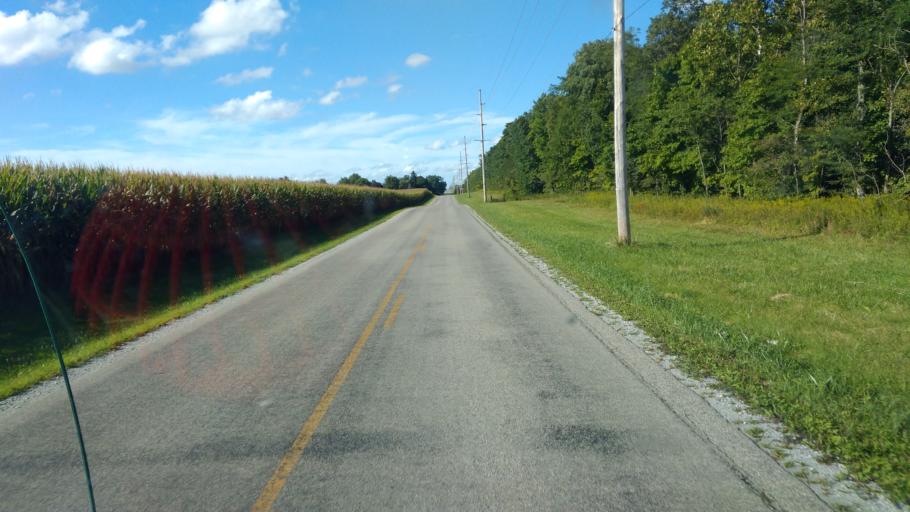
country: US
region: Ohio
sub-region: Hardin County
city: Kenton
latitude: 40.7105
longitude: -83.6534
